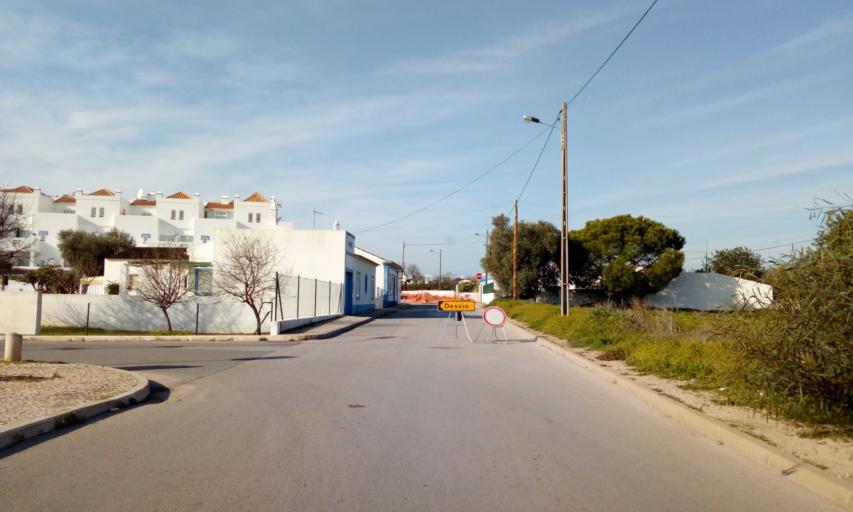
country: PT
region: Faro
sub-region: Tavira
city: Tavira
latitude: 37.1419
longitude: -7.5995
